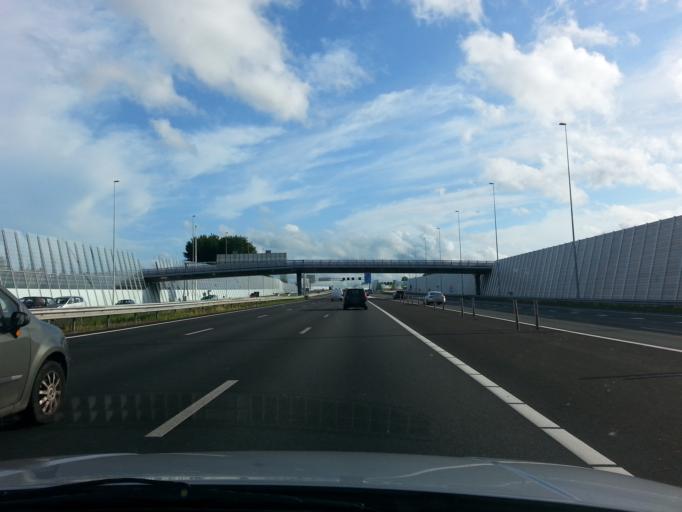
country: NL
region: North Holland
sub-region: Gemeente Diemen
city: Diemen
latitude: 52.3438
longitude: 4.9568
